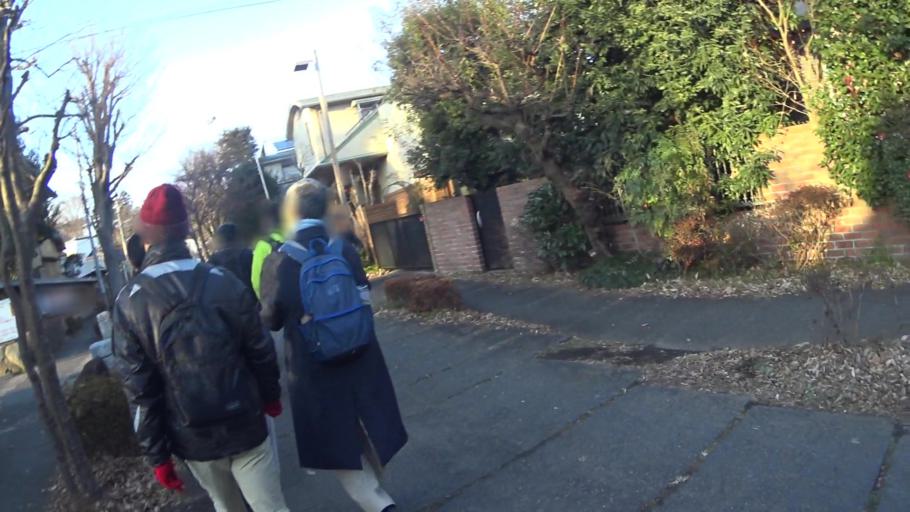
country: JP
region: Saitama
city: Saitama
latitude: 35.9250
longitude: 139.6318
